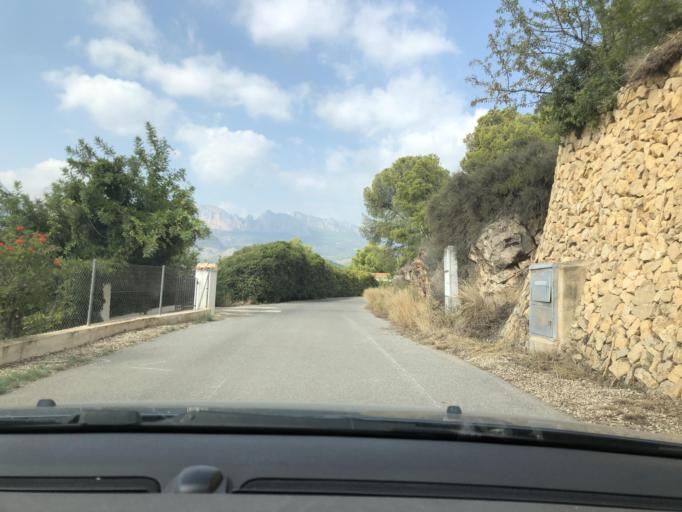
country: ES
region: Valencia
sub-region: Provincia de Alicante
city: Callosa d'En Sarria
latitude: 38.6326
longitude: -0.1107
